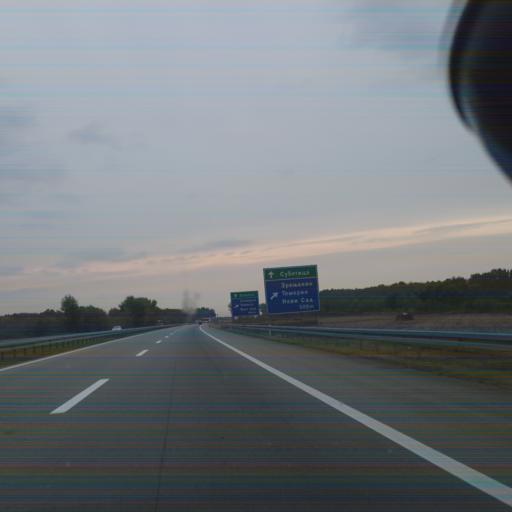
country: RS
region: Autonomna Pokrajina Vojvodina
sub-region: Juznobacki Okrug
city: Petrovaradin
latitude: 45.2826
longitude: 19.9021
